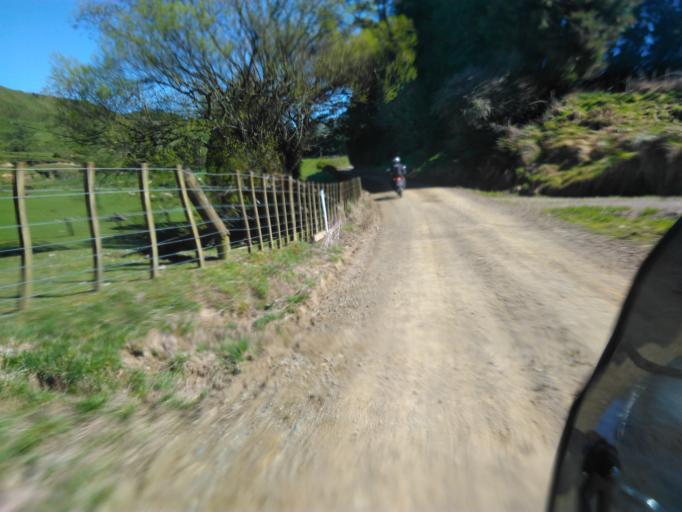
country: NZ
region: Bay of Plenty
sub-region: Opotiki District
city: Opotiki
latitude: -38.2932
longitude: 177.5488
